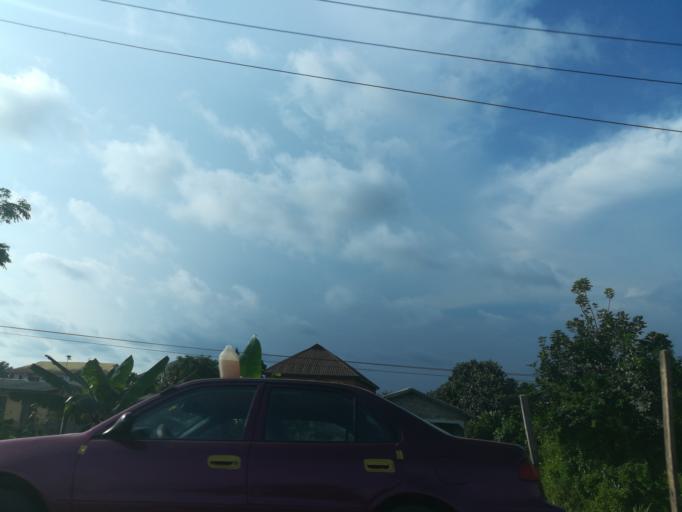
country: NG
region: Ogun
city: Ado Odo
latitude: 6.4940
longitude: 3.0821
